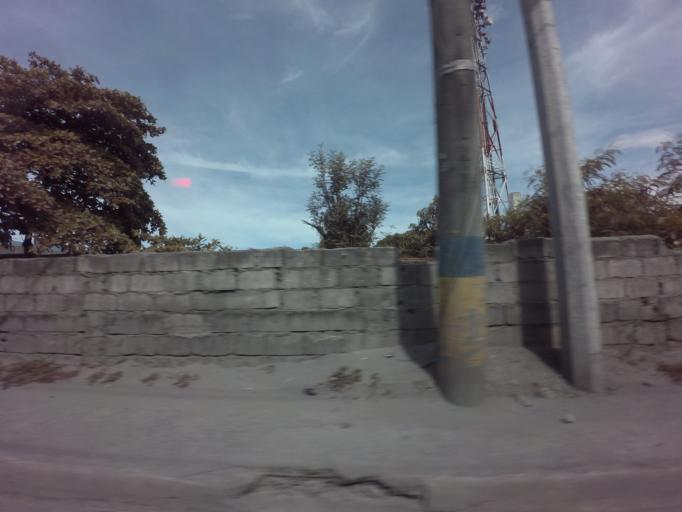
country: PH
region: Calabarzon
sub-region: Province of Rizal
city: Pateros
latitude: 14.5434
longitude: 121.0886
